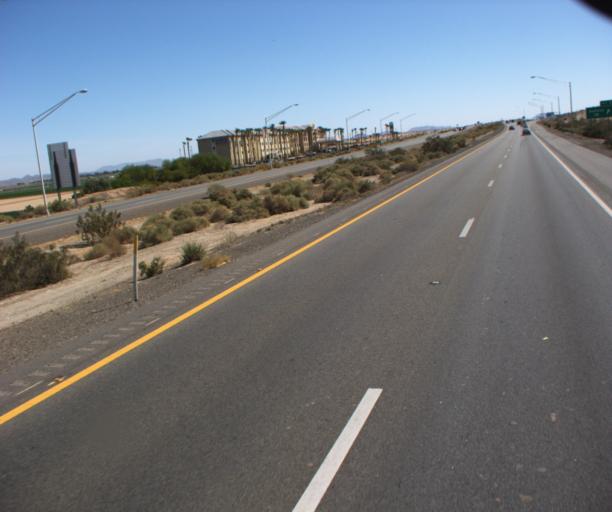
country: US
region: Arizona
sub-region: Yuma County
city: Yuma
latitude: 32.6905
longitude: -114.5903
